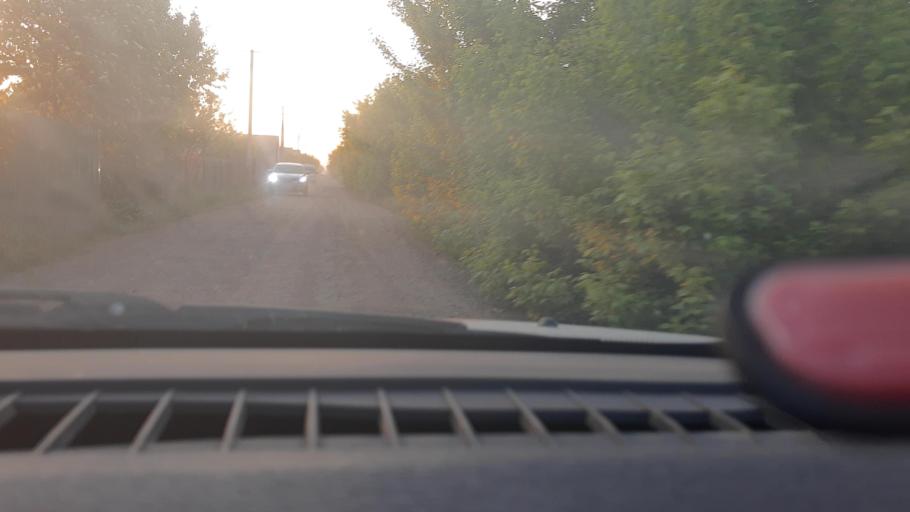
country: RU
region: Bashkortostan
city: Ufa
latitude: 54.5540
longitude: 55.9298
